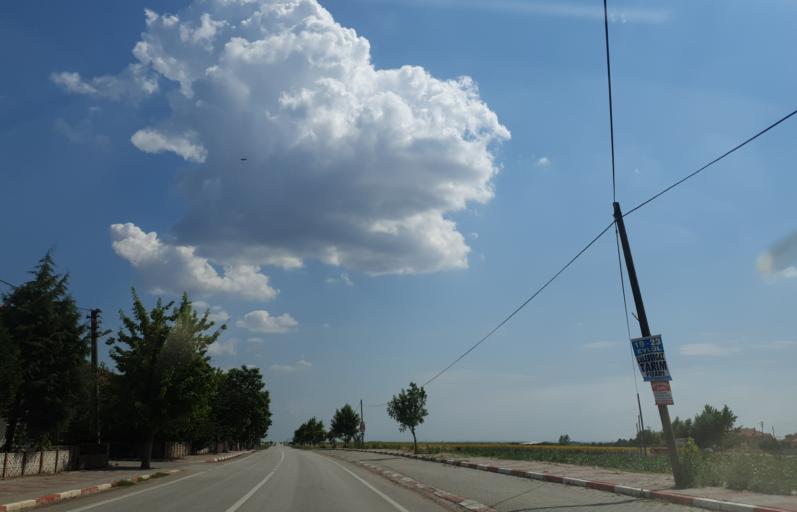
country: TR
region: Kirklareli
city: Buyukkaristiran
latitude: 41.4353
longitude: 27.5837
